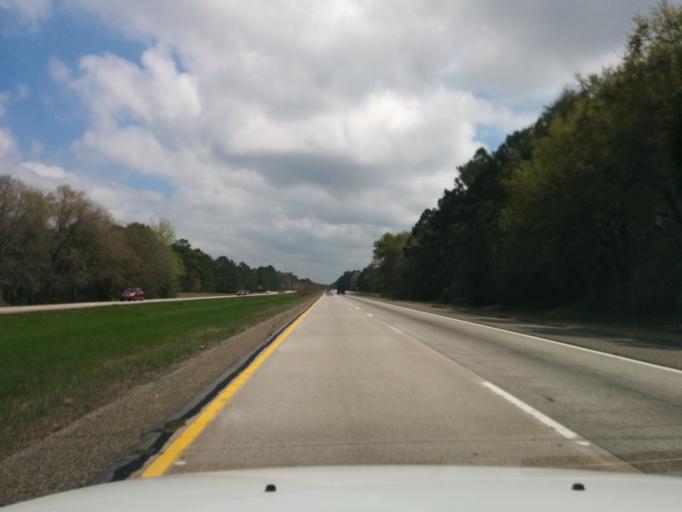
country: US
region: Georgia
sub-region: Bryan County
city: Pembroke
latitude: 32.2192
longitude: -81.5388
